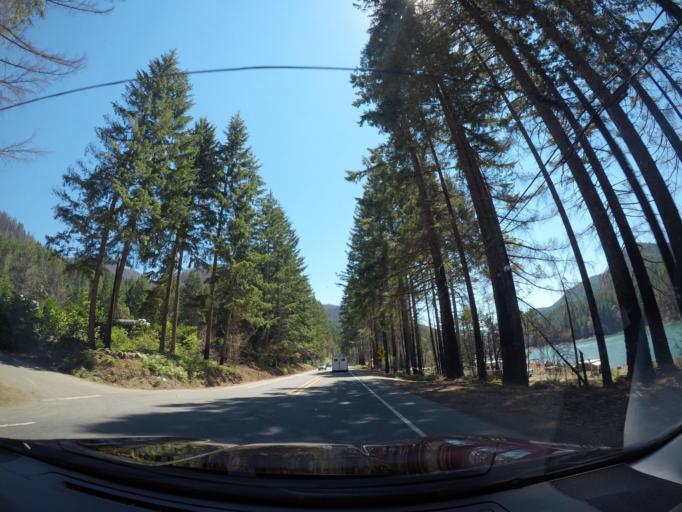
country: US
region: Oregon
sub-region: Linn County
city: Mill City
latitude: 44.7291
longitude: -122.1438
